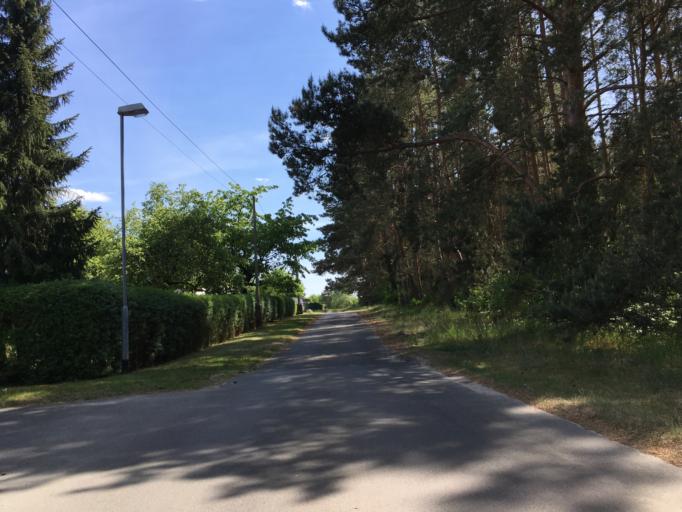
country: DE
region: Brandenburg
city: Oderberg
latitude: 52.8411
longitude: 14.1170
